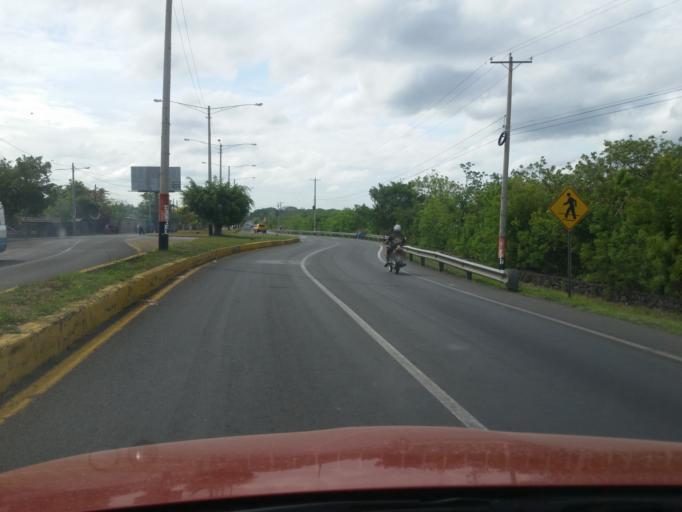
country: NI
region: Masaya
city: Nindiri
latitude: 12.0221
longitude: -86.1553
